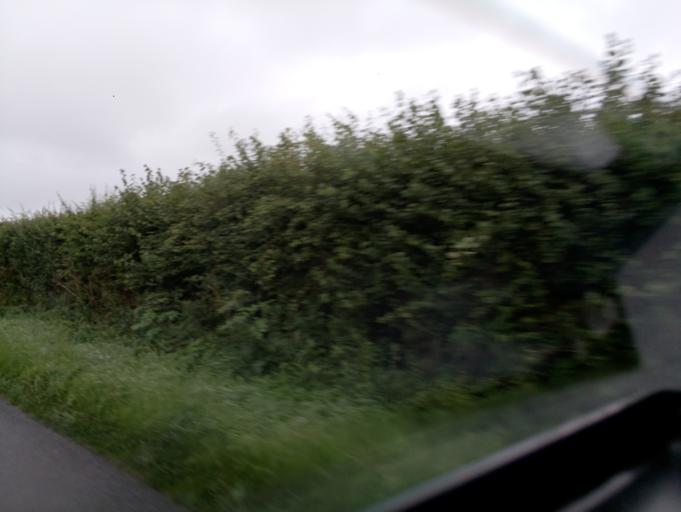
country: GB
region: England
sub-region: Gloucestershire
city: Uckington
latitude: 51.9260
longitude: -2.1205
